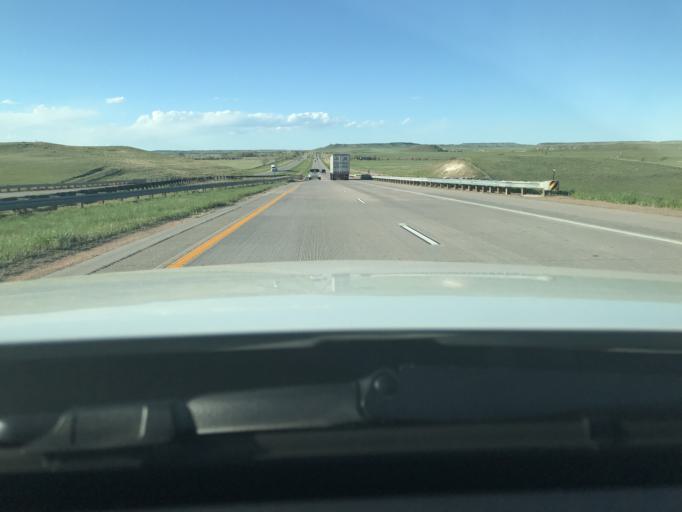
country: US
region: Wyoming
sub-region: Laramie County
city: South Greeley
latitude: 40.9348
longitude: -104.9290
